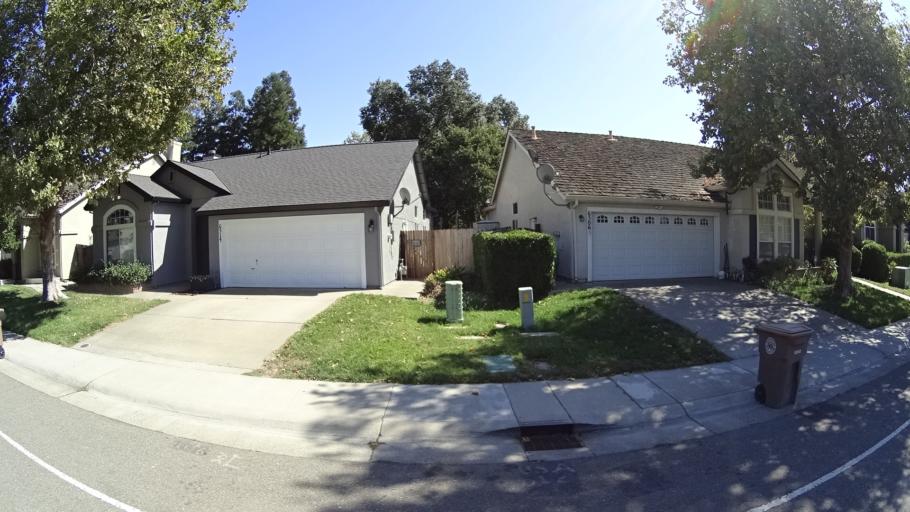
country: US
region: California
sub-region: Sacramento County
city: Laguna
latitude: 38.4267
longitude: -121.4262
